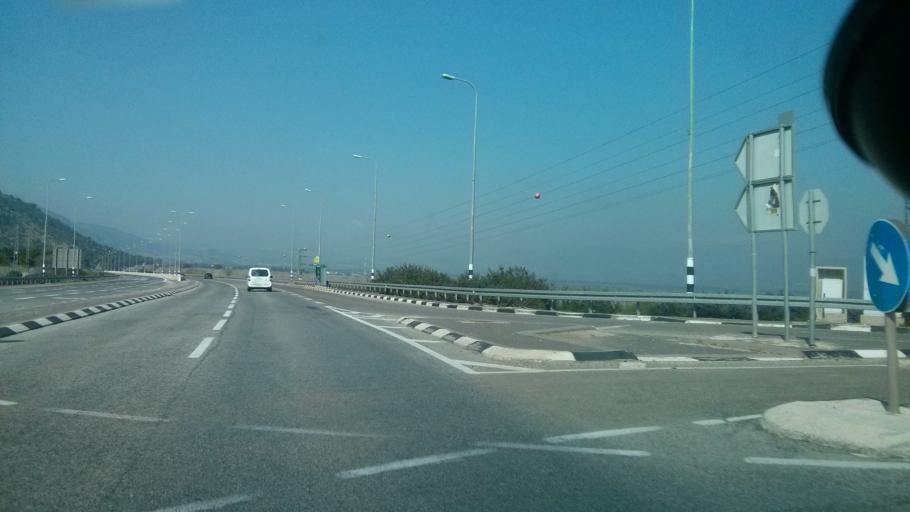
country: IL
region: Northern District
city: Rosh Pinna
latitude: 33.0720
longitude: 35.5765
